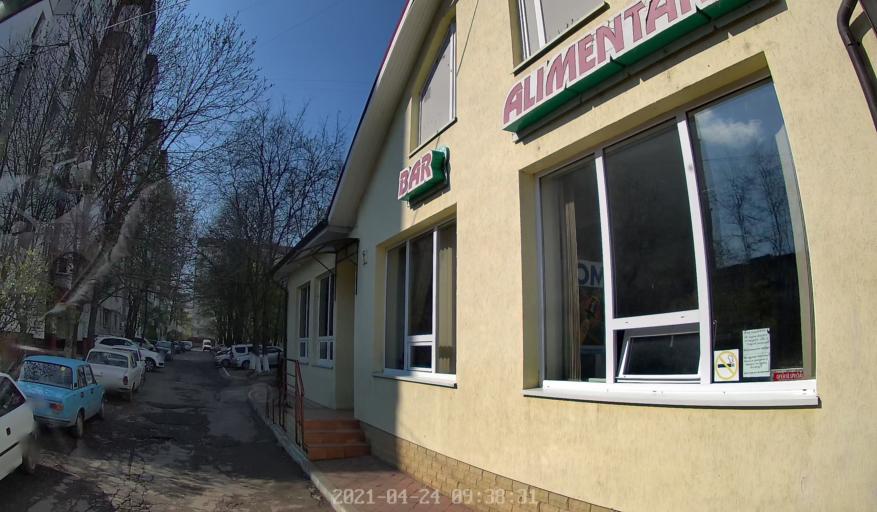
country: MD
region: Chisinau
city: Chisinau
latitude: 47.0447
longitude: 28.8962
